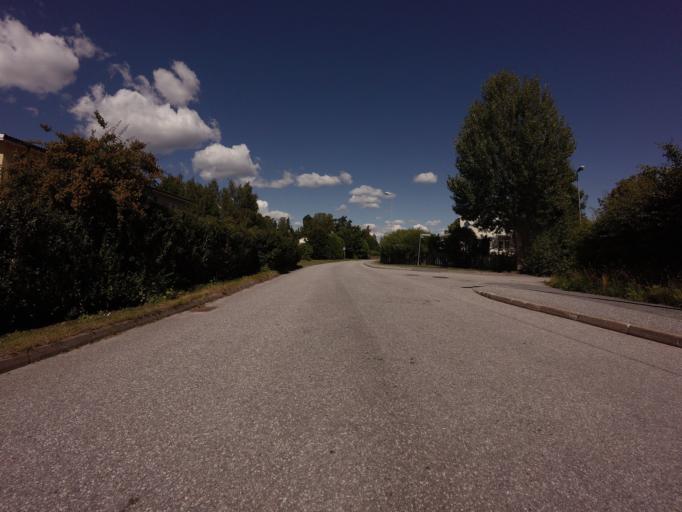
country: SE
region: Stockholm
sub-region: Sollentuna Kommun
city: Sollentuna
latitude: 59.4522
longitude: 17.9026
